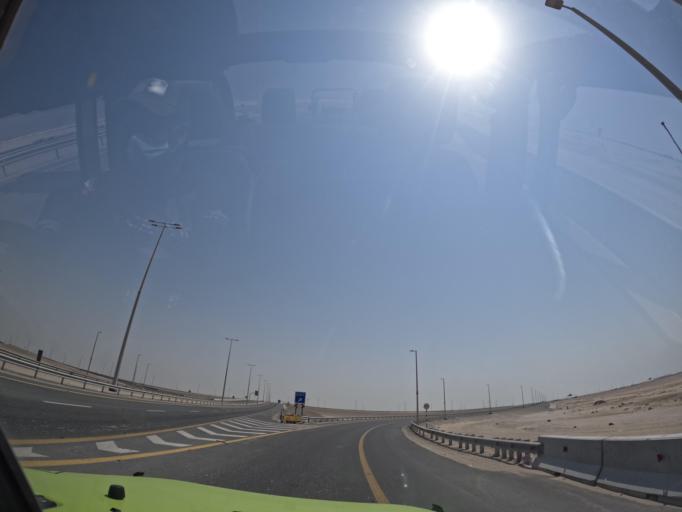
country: AE
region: Abu Dhabi
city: Abu Dhabi
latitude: 24.2502
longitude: 54.4693
